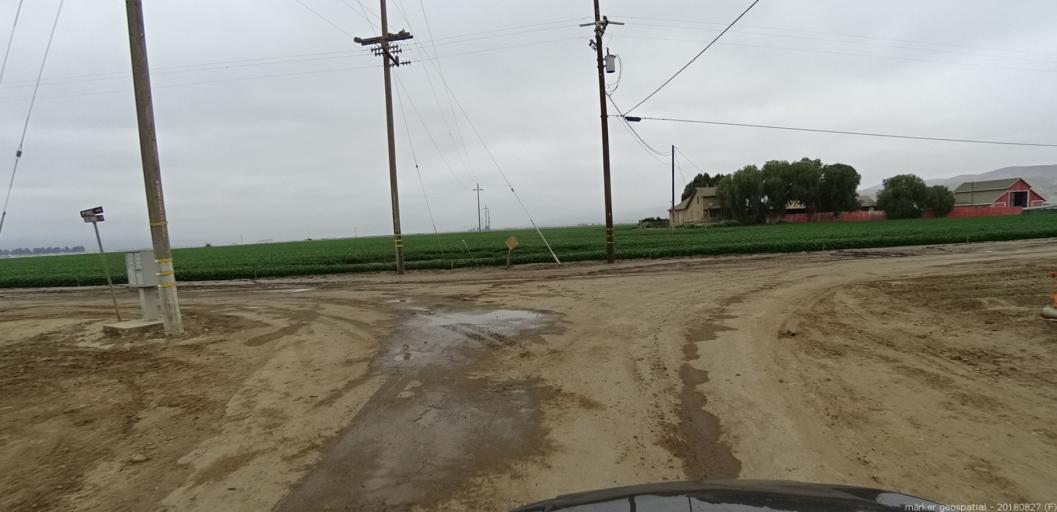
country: US
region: California
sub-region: Monterey County
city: Greenfield
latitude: 36.3419
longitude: -121.2368
